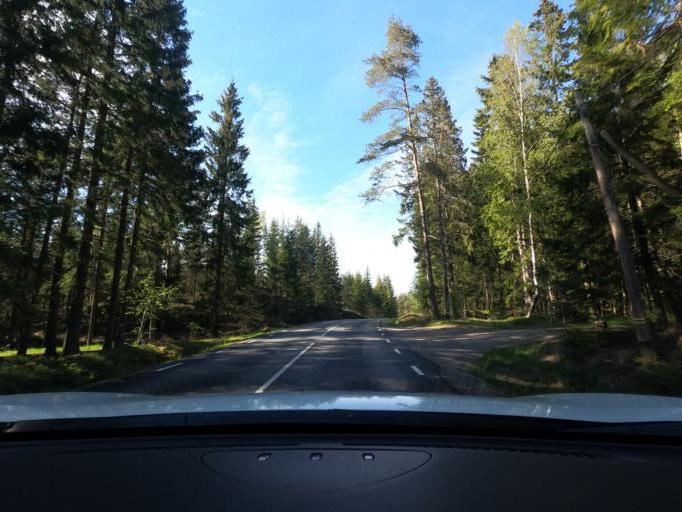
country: SE
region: Vaestra Goetaland
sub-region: Harryda Kommun
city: Landvetter
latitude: 57.6247
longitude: 12.2775
